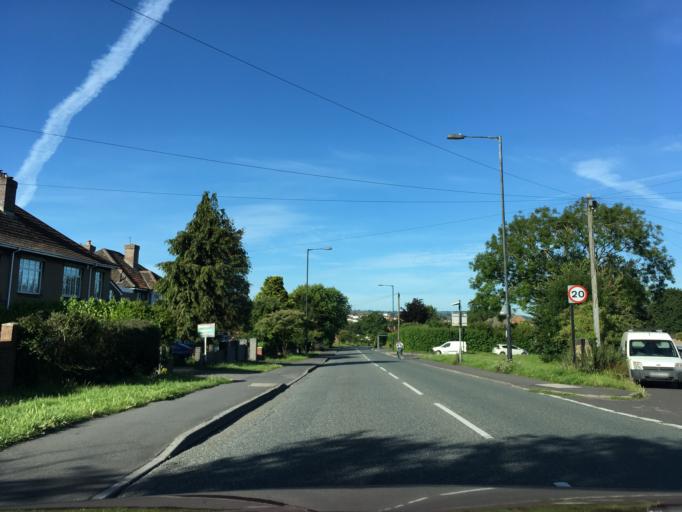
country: GB
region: England
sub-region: Bath and North East Somerset
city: Whitchurch
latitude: 51.4301
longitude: -2.5495
